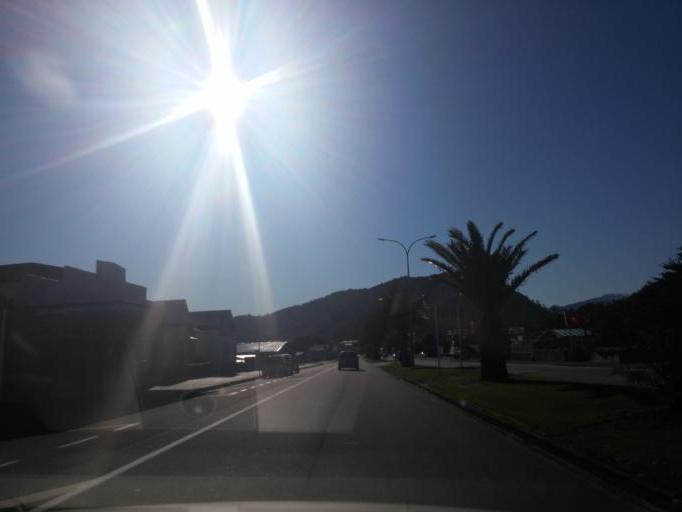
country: NZ
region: West Coast
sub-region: Grey District
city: Greymouth
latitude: -42.4540
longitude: 171.2083
